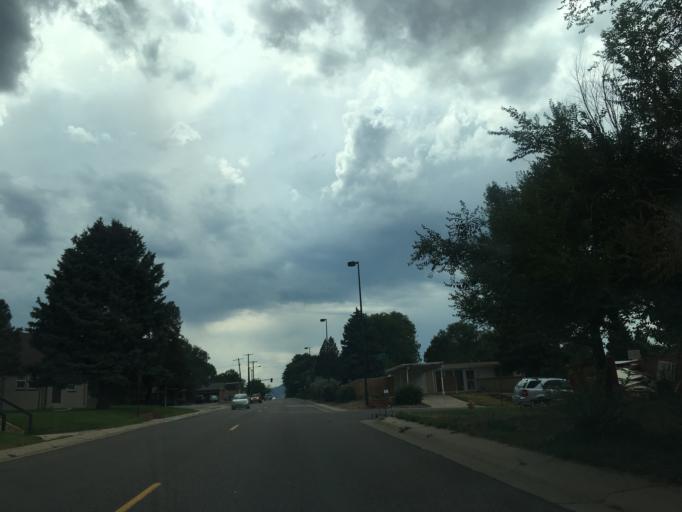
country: US
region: Colorado
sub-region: Arapahoe County
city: Sheridan
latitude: 39.6677
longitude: -105.0394
